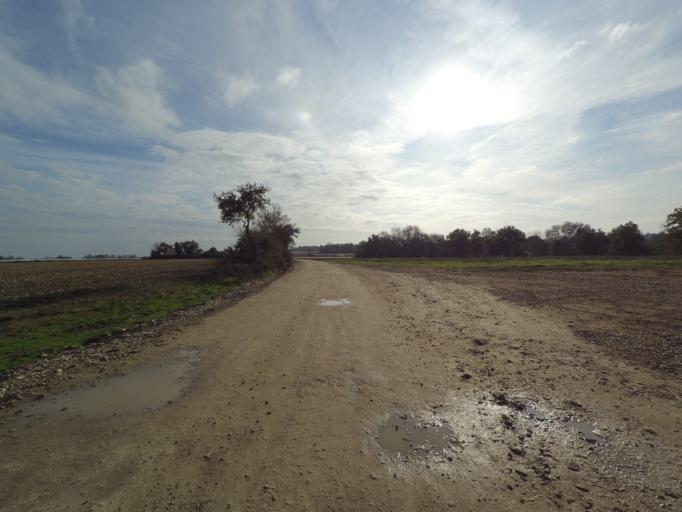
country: FR
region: Pays de la Loire
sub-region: Departement de la Vendee
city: Saint-Hilaire-de-Loulay
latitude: 47.0072
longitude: -1.3627
